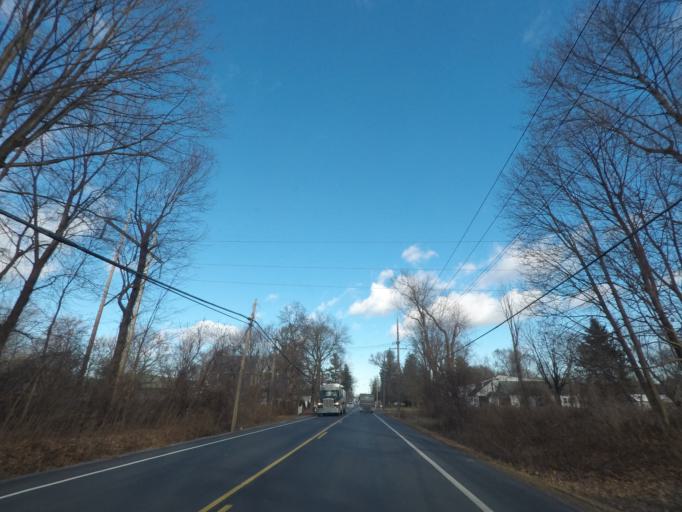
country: US
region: New York
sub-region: Saratoga County
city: Waterford
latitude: 42.8219
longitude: -73.6669
